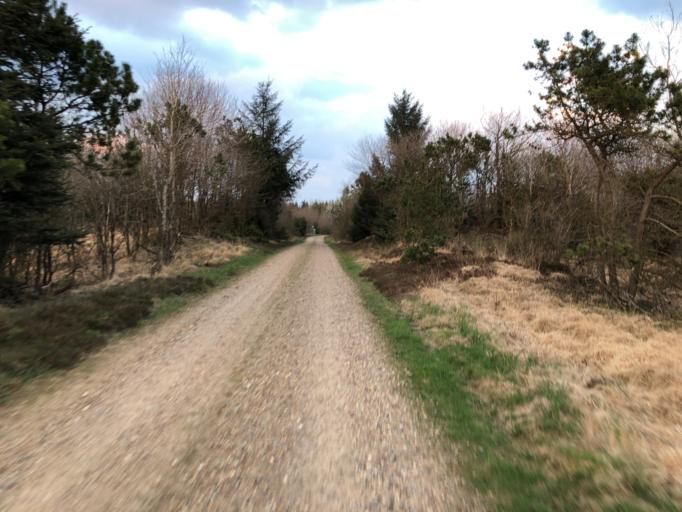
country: DK
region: Central Jutland
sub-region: Holstebro Kommune
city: Ulfborg
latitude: 56.2247
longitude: 8.4287
